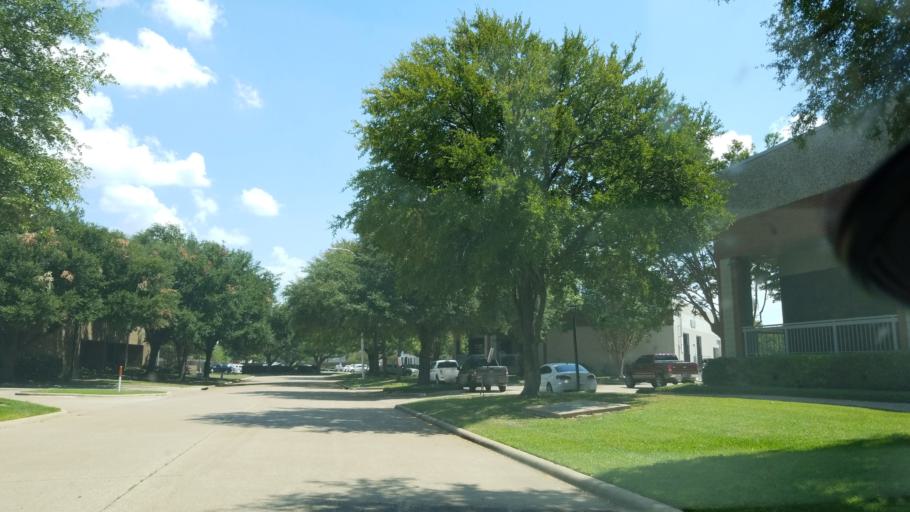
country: US
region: Texas
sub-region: Dallas County
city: Richardson
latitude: 32.8928
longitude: -96.7041
